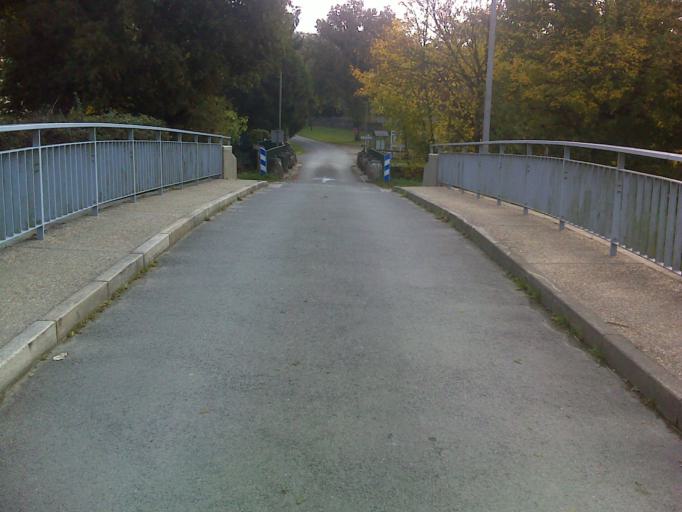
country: FR
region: Brittany
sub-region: Departement du Morbihan
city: Rieux
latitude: 47.5993
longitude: -2.0908
